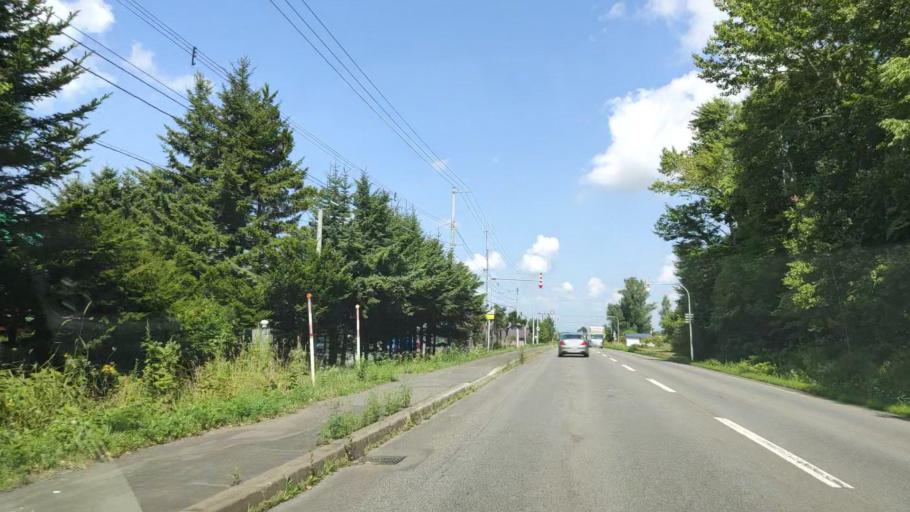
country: JP
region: Hokkaido
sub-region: Asahikawa-shi
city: Asahikawa
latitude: 43.6347
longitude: 142.4567
